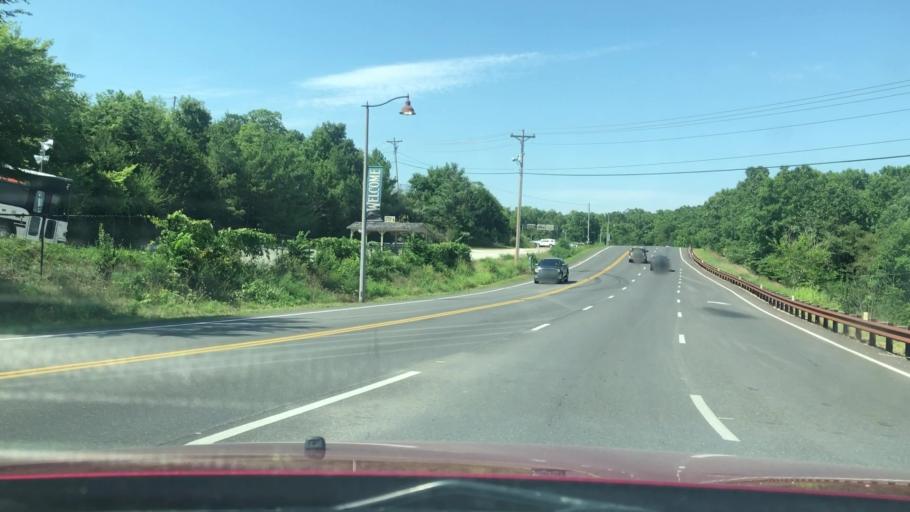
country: US
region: Missouri
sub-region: Stone County
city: Kimberling City
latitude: 36.6618
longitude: -93.3373
